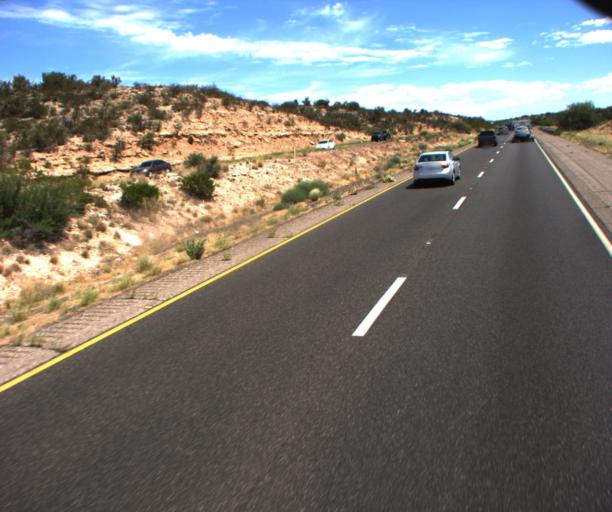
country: US
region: Arizona
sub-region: Yavapai County
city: Lake Montezuma
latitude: 34.6475
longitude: -111.8027
